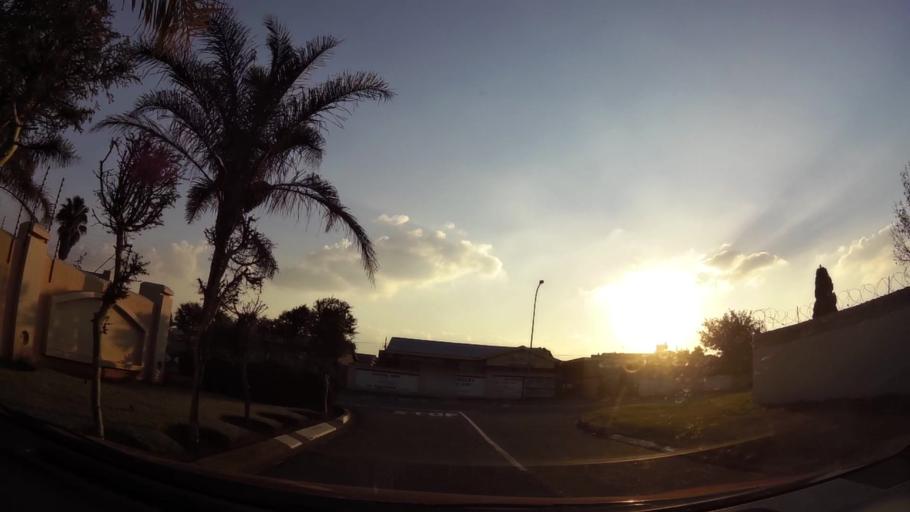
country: ZA
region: Gauteng
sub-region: City of Johannesburg Metropolitan Municipality
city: Soweto
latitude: -26.2824
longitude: 27.9059
